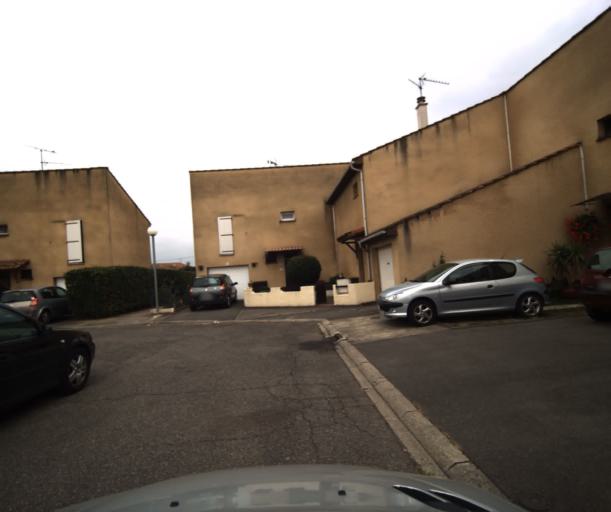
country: FR
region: Midi-Pyrenees
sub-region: Departement de la Haute-Garonne
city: Portet-sur-Garonne
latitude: 43.5382
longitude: 1.4062
